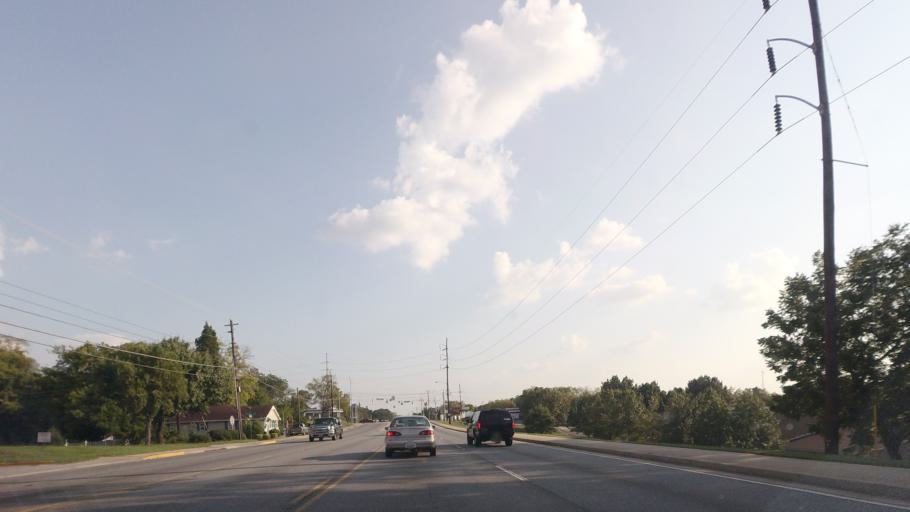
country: US
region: Georgia
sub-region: Bibb County
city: Macon
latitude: 32.8272
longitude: -83.6628
